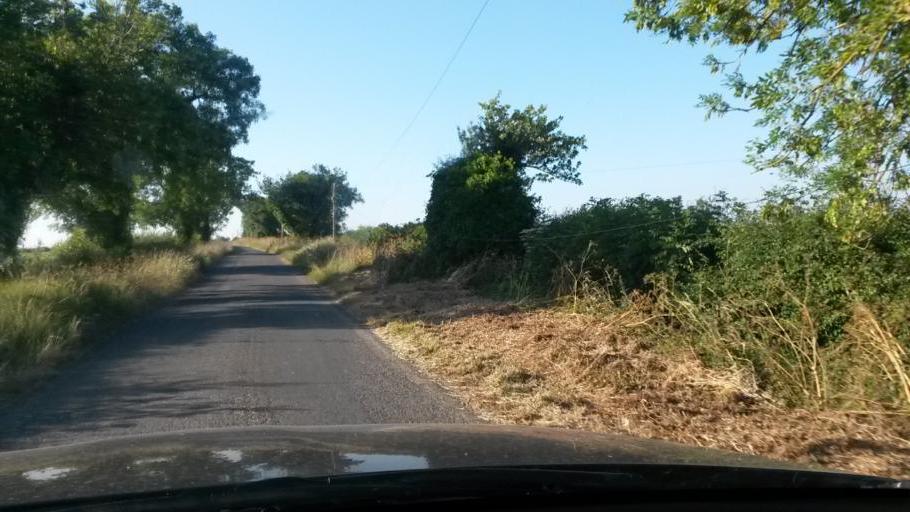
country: IE
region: Leinster
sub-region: Fingal County
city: Swords
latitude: 53.5037
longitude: -6.2939
